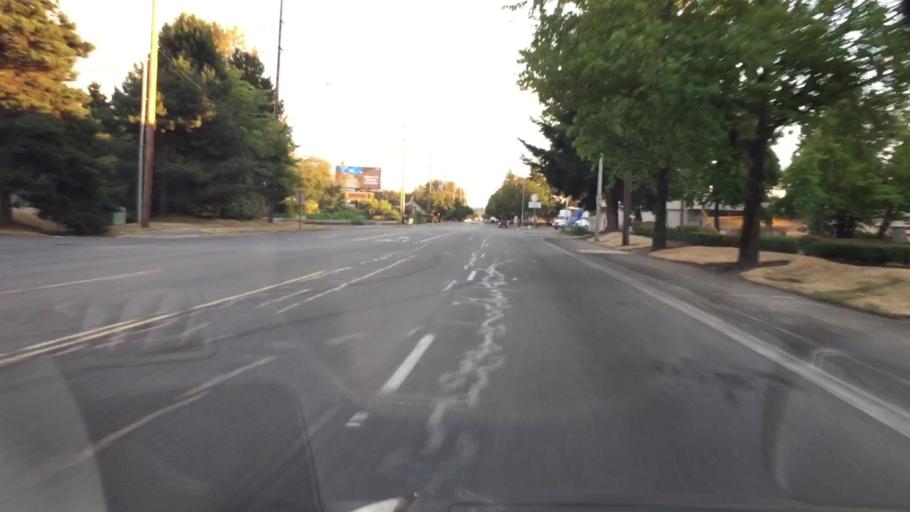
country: US
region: Washington
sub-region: King County
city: Renton
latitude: 47.4324
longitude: -122.2281
